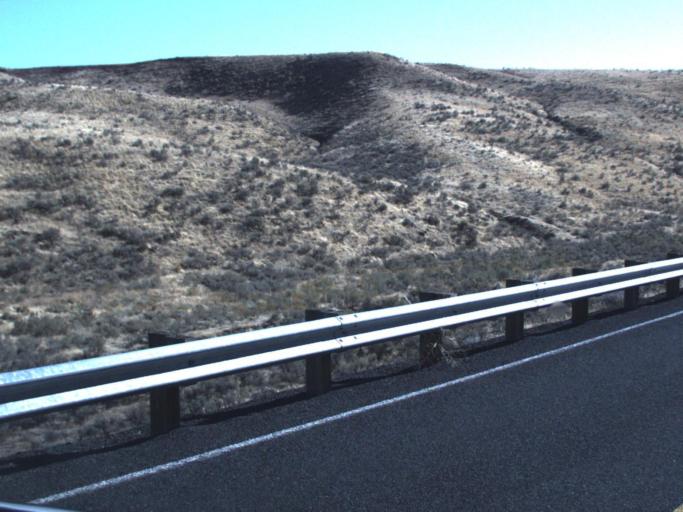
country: US
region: Washington
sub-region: Franklin County
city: Connell
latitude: 46.6573
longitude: -118.5491
